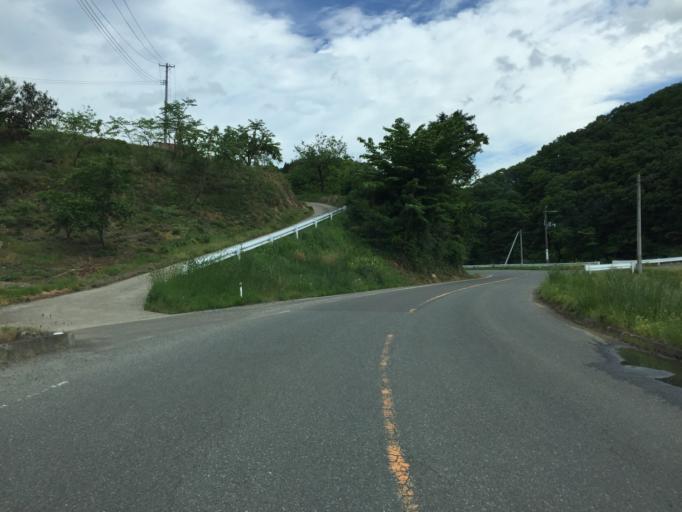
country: JP
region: Fukushima
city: Nihommatsu
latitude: 37.6362
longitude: 140.4961
